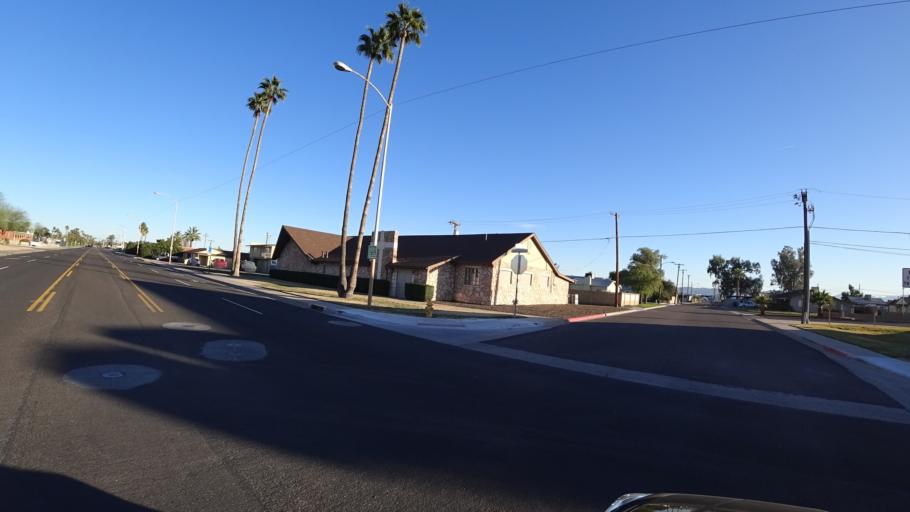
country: US
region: Arizona
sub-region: Maricopa County
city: Phoenix
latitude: 33.4733
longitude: -112.1043
